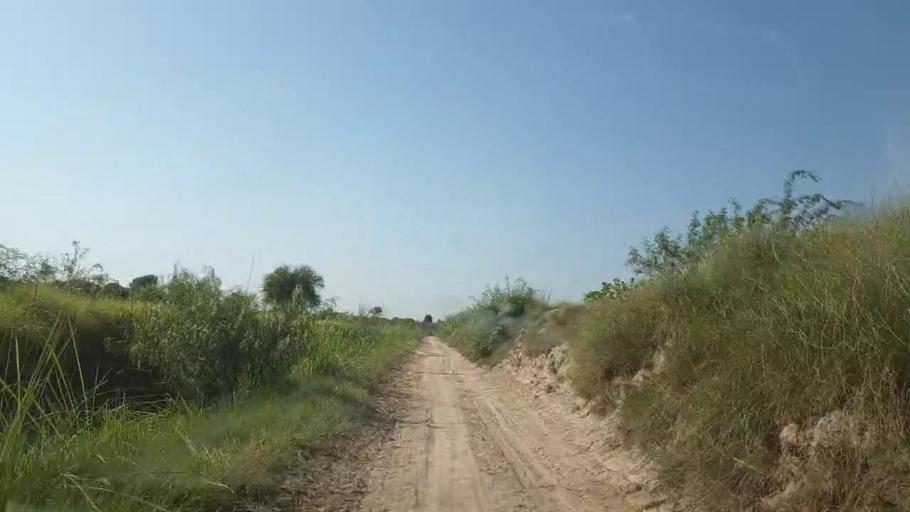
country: PK
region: Sindh
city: Tando Jam
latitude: 25.3201
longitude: 68.6005
